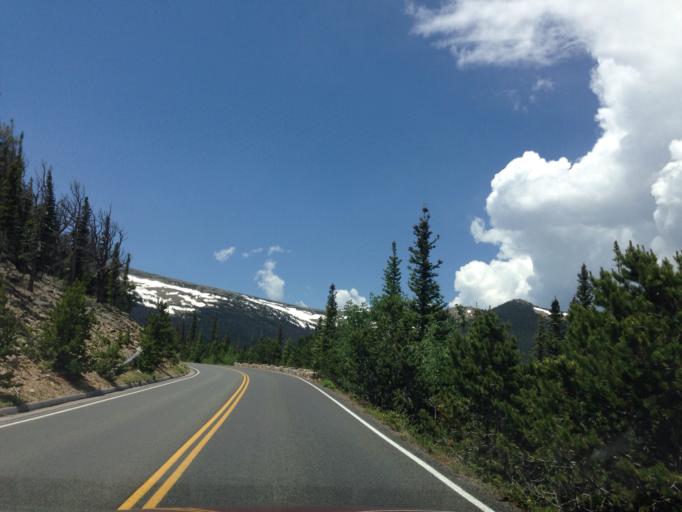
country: US
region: Colorado
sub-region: Larimer County
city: Estes Park
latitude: 40.3945
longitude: -105.6447
